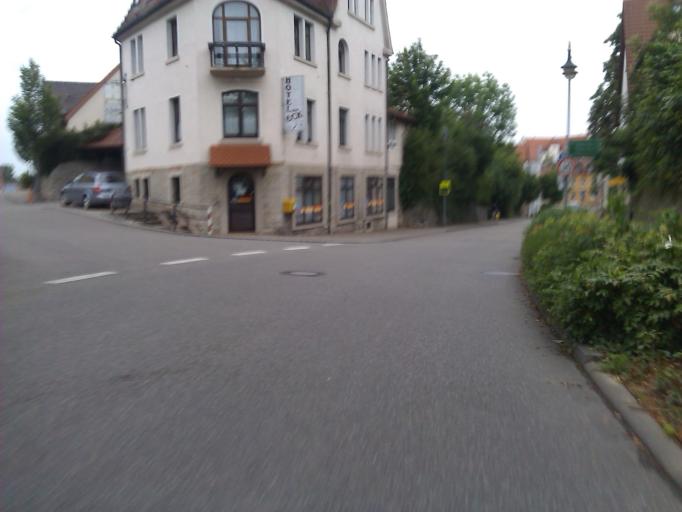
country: DE
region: Baden-Wuerttemberg
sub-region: Regierungsbezirk Stuttgart
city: Untereisesheim
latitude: 49.2215
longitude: 9.2154
